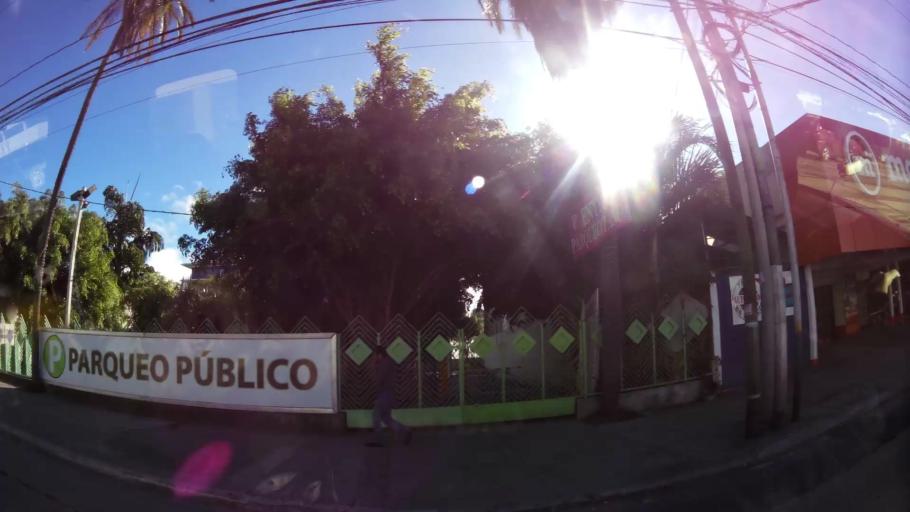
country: GT
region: Guatemala
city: Guatemala City
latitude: 14.6034
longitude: -90.5202
